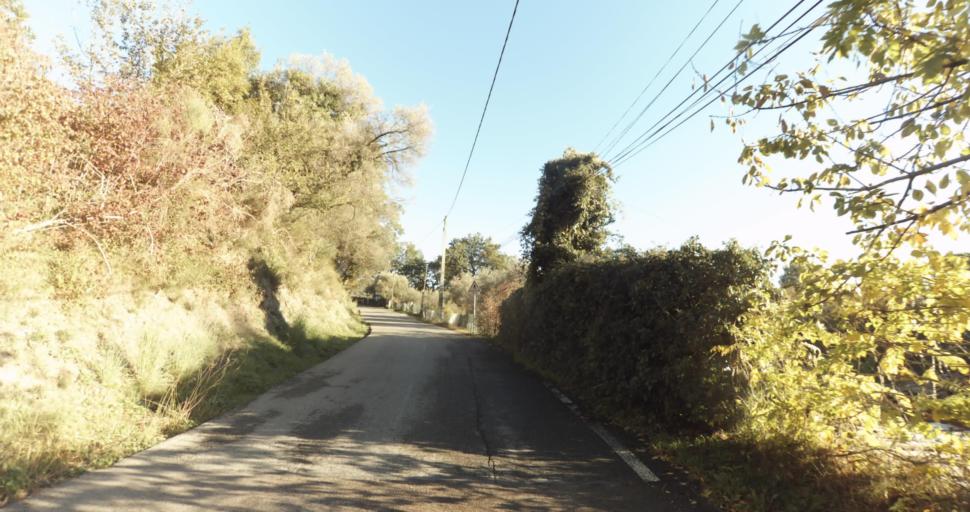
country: FR
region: Provence-Alpes-Cote d'Azur
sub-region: Departement des Alpes-Maritimes
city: Vence
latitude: 43.7339
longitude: 7.1276
